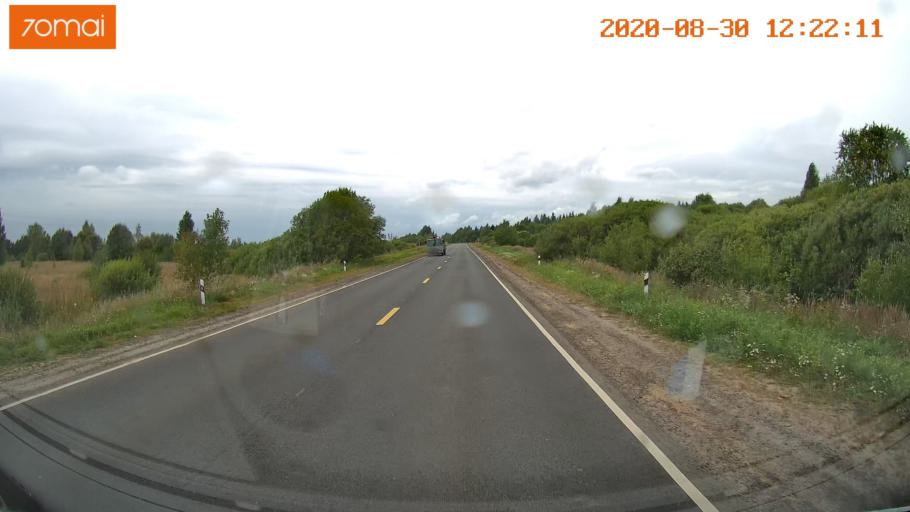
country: RU
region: Ivanovo
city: Yur'yevets
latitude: 57.3289
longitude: 42.8563
